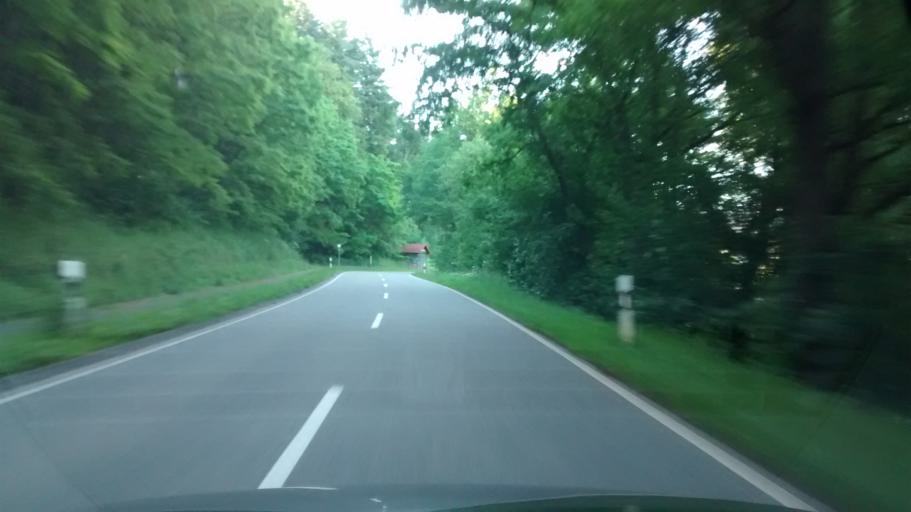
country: DE
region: Rheinland-Pfalz
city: Erfweiler
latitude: 49.1465
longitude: 7.8072
